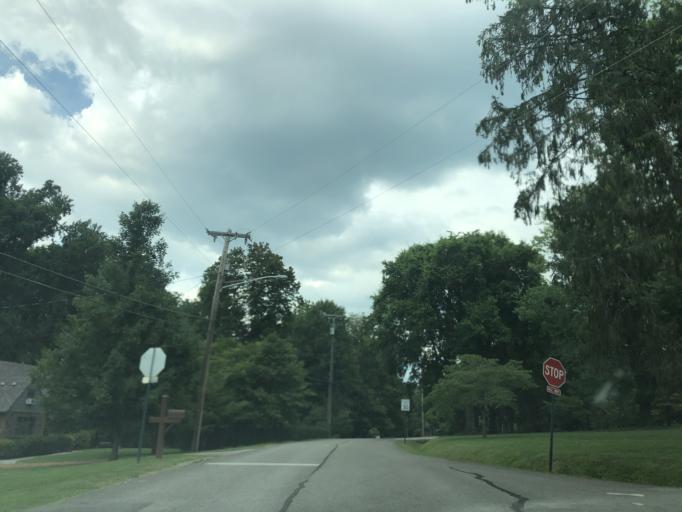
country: US
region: Tennessee
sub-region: Davidson County
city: Lakewood
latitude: 36.1666
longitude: -86.6737
